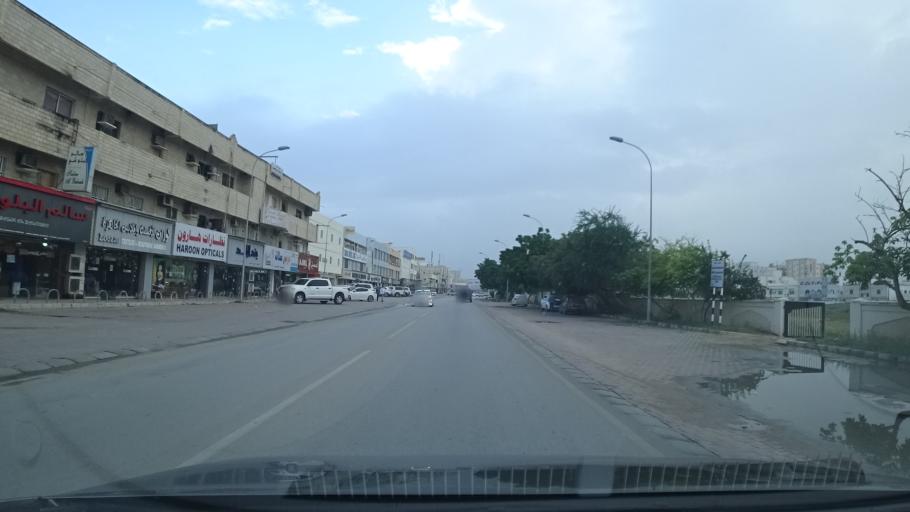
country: OM
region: Zufar
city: Salalah
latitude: 17.0111
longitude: 54.0885
